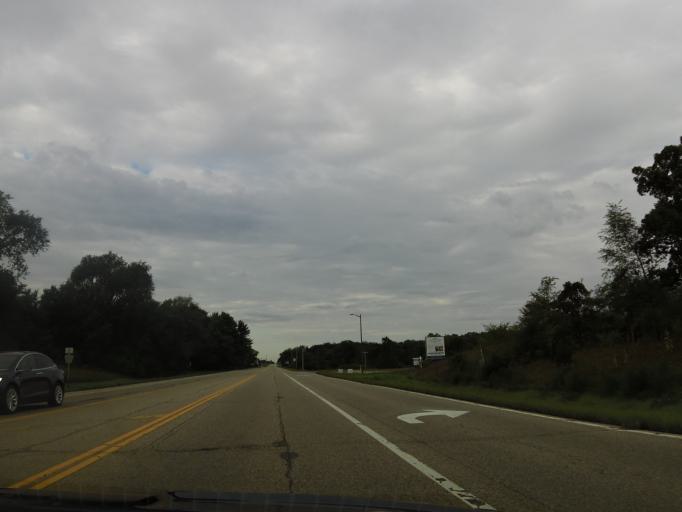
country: US
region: Minnesota
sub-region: Dakota County
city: Hastings
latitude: 44.7167
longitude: -92.8908
